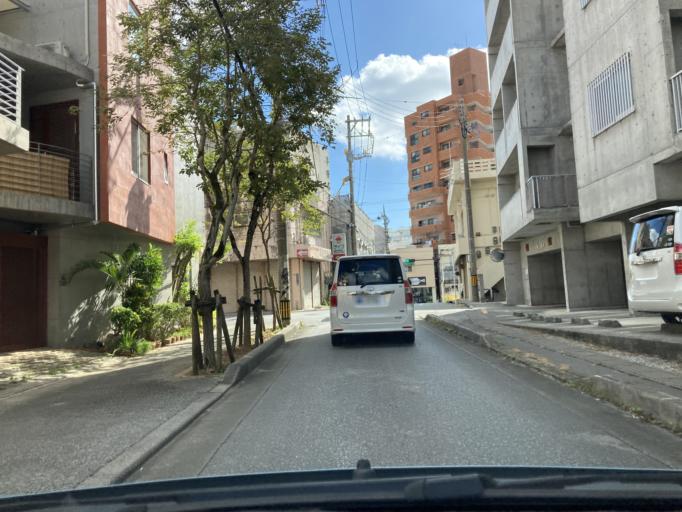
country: JP
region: Okinawa
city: Okinawa
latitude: 26.3380
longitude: 127.8019
